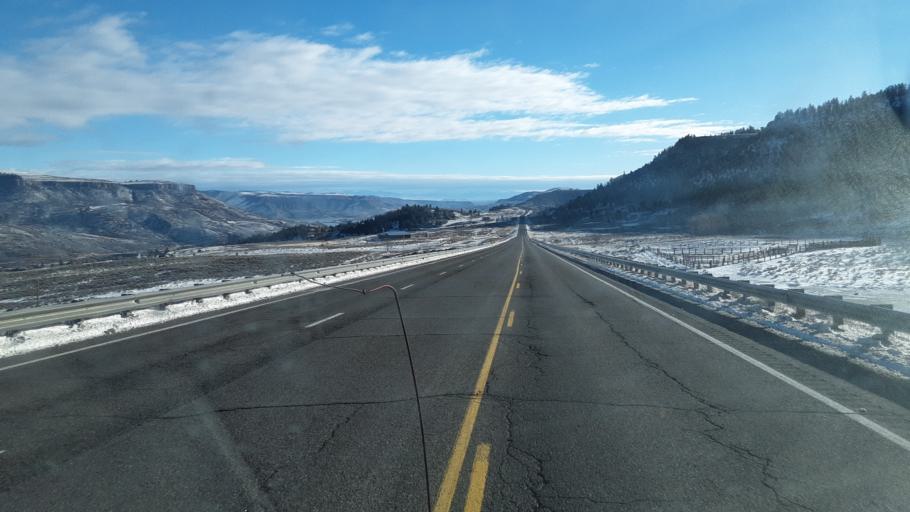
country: US
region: Colorado
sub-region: Hinsdale County
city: Lake City
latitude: 38.4375
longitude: -107.3941
